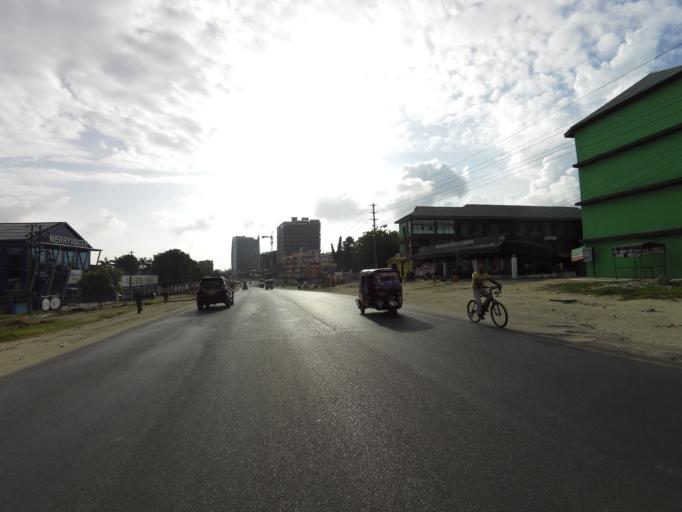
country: TZ
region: Dar es Salaam
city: Magomeni
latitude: -6.7779
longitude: 39.2497
